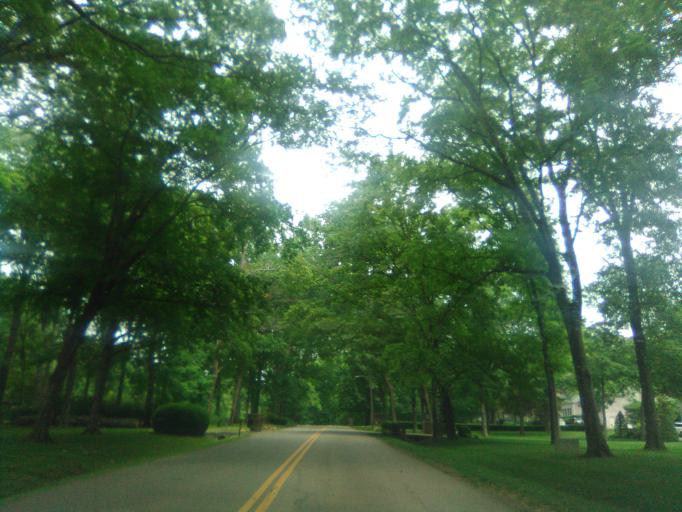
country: US
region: Tennessee
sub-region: Davidson County
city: Belle Meade
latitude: 36.1128
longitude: -86.8752
